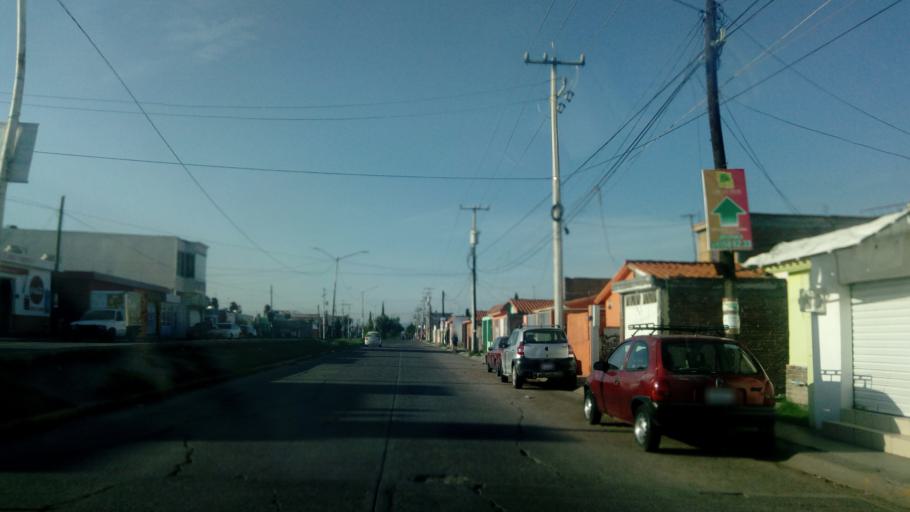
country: MX
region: Durango
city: Victoria de Durango
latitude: 24.0627
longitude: -104.5854
